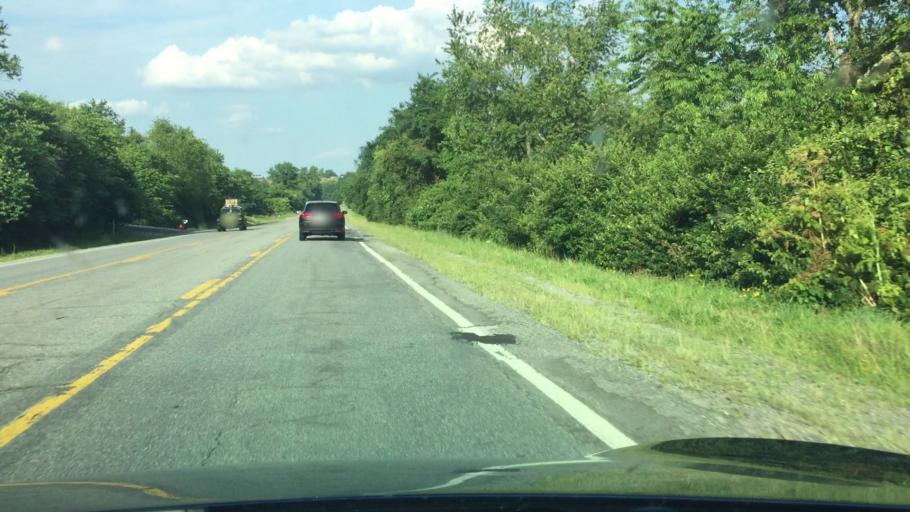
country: US
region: Virginia
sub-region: City of Radford
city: Radford
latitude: 37.1326
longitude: -80.6270
